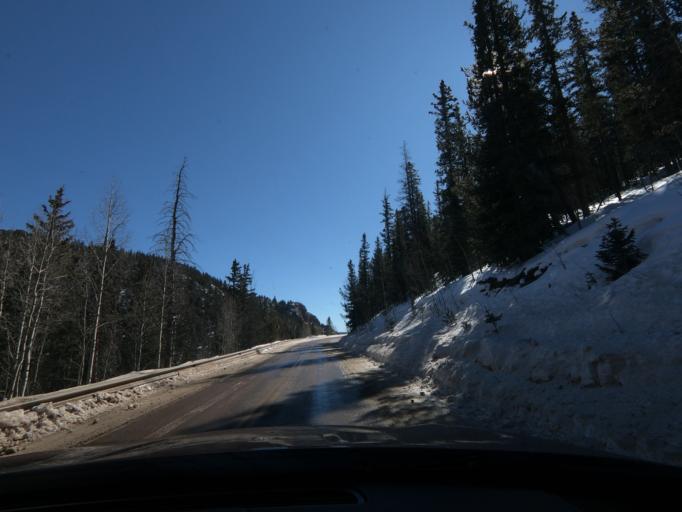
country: US
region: Colorado
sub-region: Teller County
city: Cripple Creek
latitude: 38.7483
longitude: -105.1012
